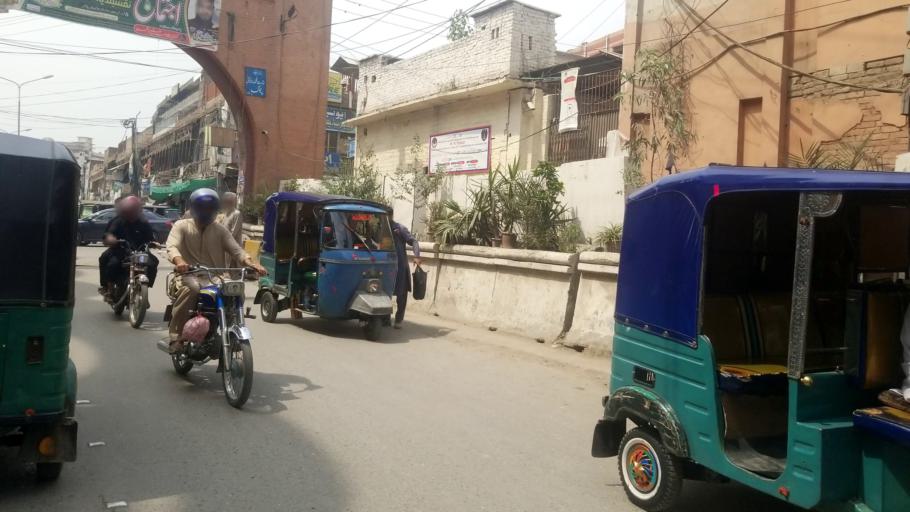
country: PK
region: Khyber Pakhtunkhwa
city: Peshawar
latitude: 34.0083
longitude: 71.5689
